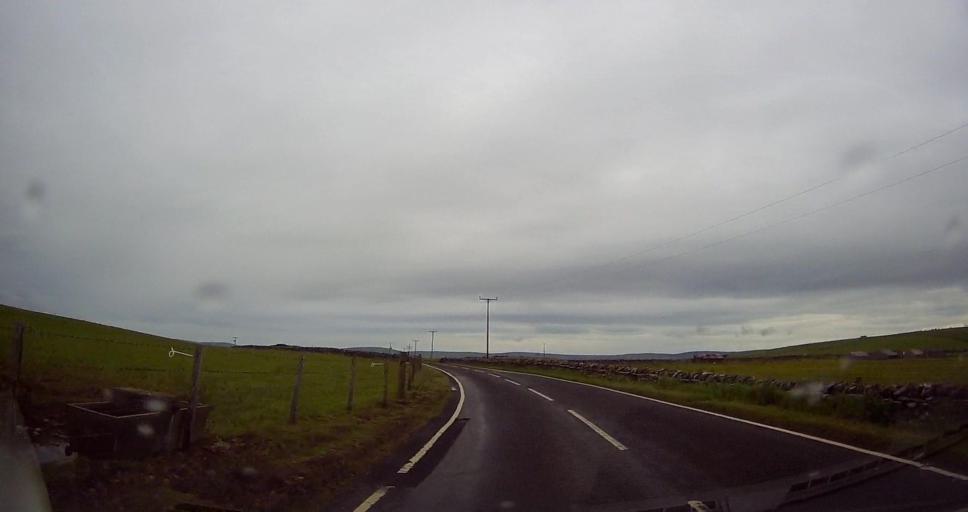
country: GB
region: Scotland
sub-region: Orkney Islands
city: Stromness
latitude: 59.0204
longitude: -3.2996
